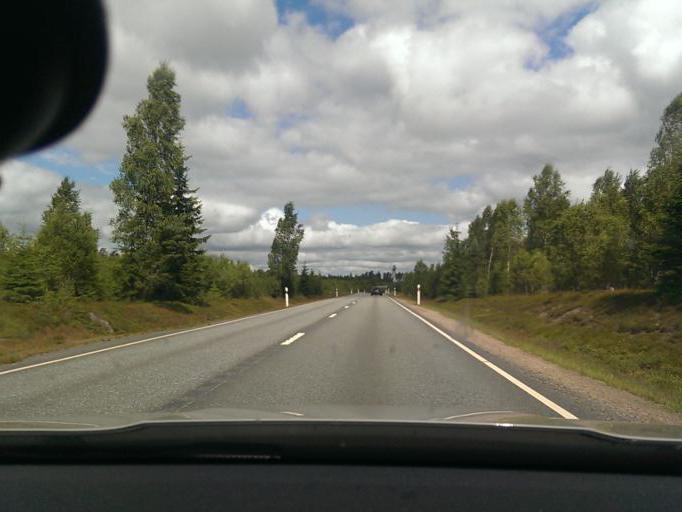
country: SE
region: Joenkoeping
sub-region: Varnamo Kommun
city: Varnamo
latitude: 57.2627
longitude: 13.9761
